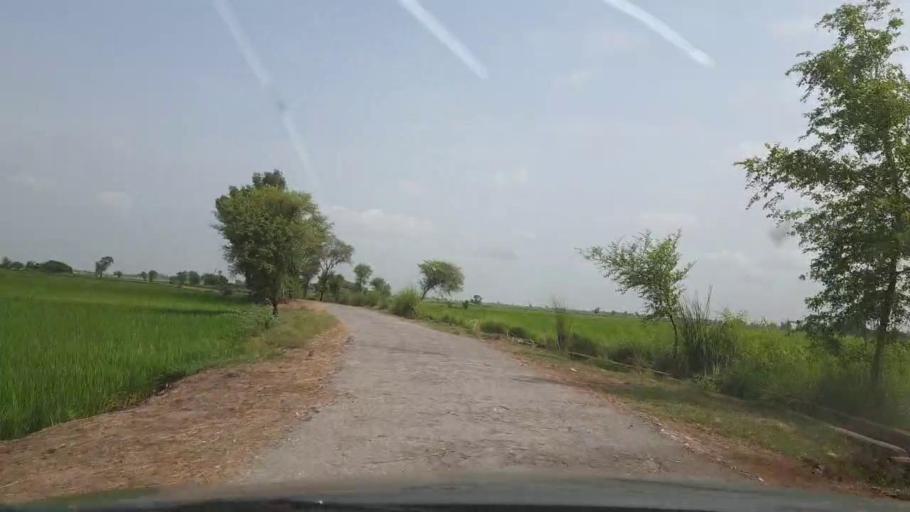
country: PK
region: Sindh
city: Ratodero
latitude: 27.8528
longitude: 68.2997
